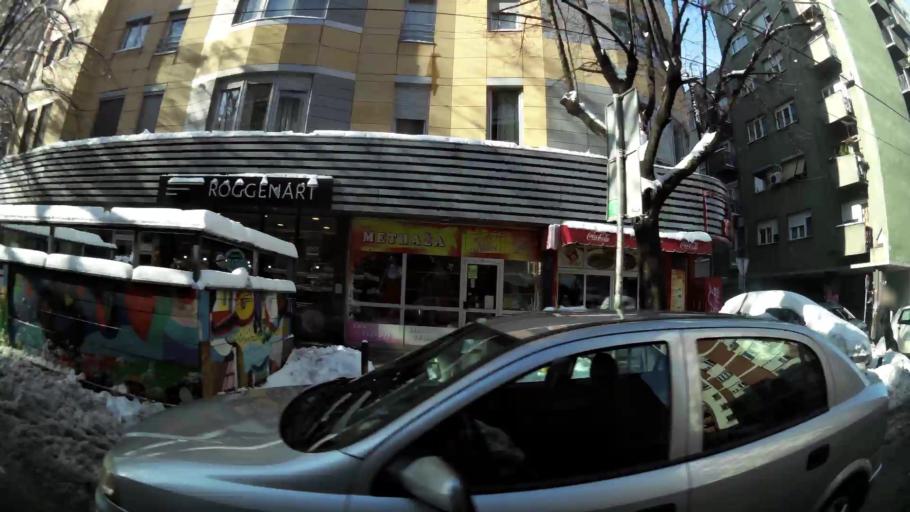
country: RS
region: Central Serbia
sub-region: Belgrade
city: Vracar
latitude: 44.7986
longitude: 20.4767
